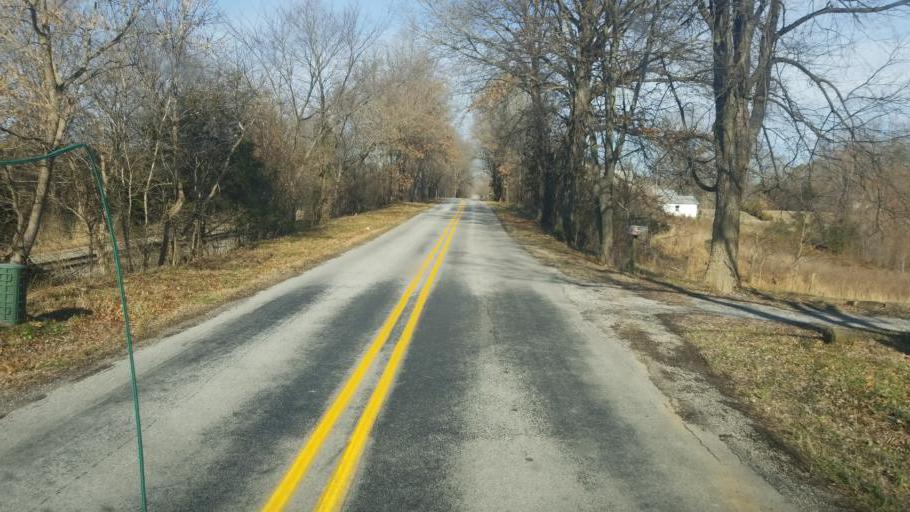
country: US
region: Illinois
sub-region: Jackson County
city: Carbondale
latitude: 37.6874
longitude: -89.2109
